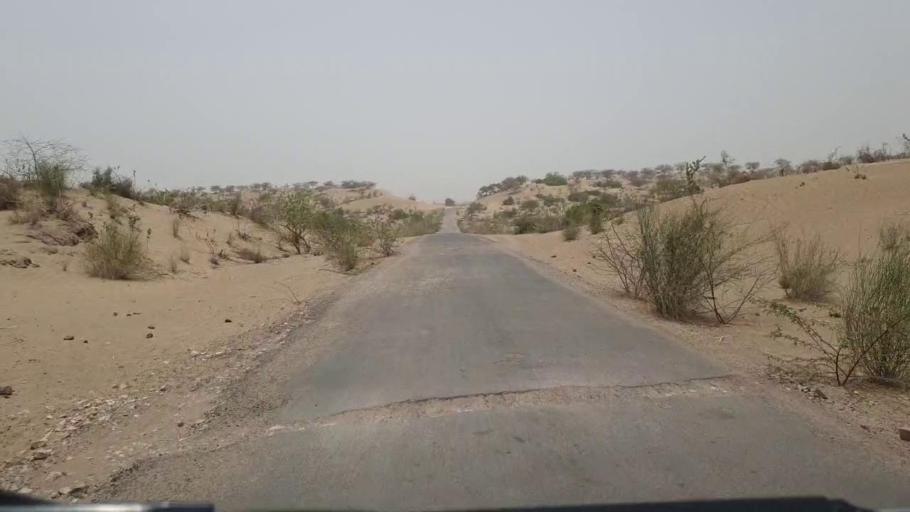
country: PK
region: Sindh
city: Naukot
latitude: 24.7587
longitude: 69.5506
